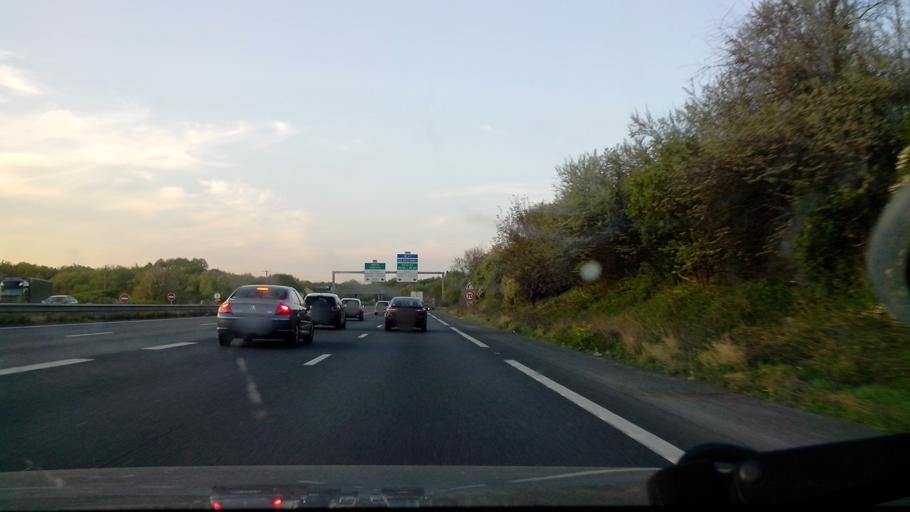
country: FR
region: Ile-de-France
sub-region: Departement de Seine-et-Marne
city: Lieusaint
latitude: 48.6395
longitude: 2.5356
